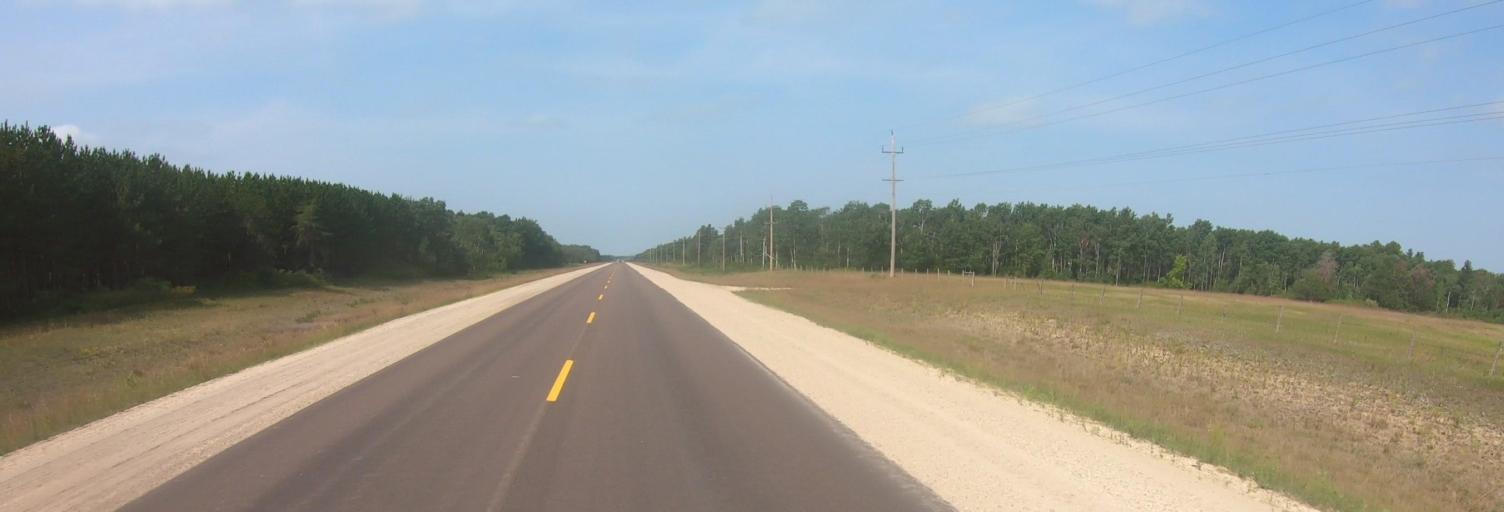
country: CA
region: Manitoba
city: La Broquerie
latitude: 49.2669
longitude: -96.4346
